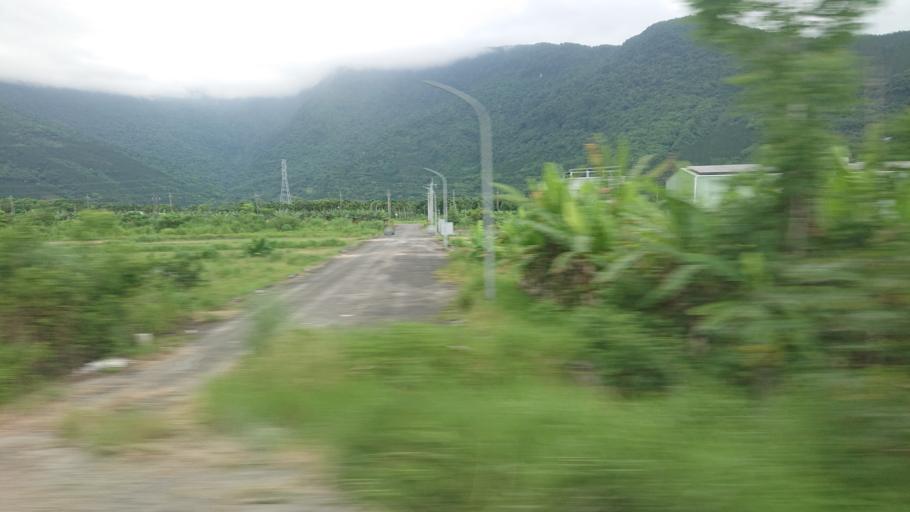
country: TW
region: Taiwan
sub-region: Hualien
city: Hualian
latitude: 23.7528
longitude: 121.4501
